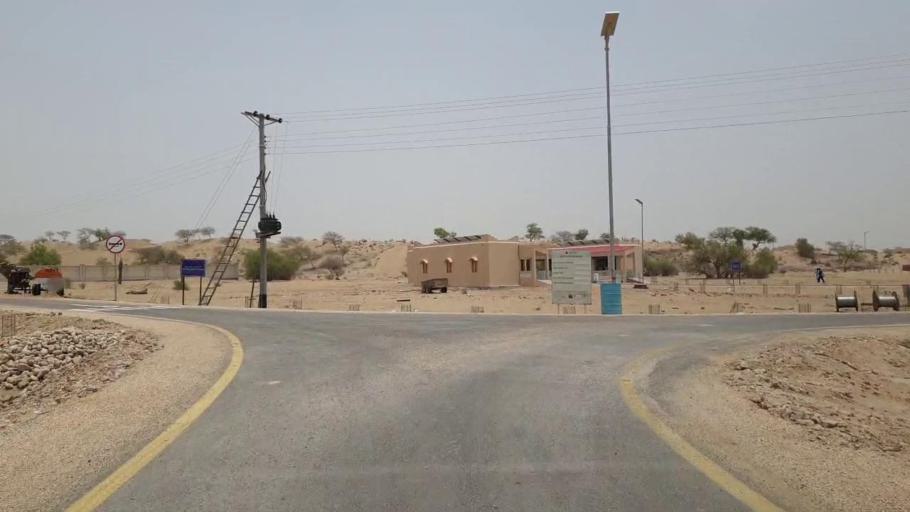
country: PK
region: Sindh
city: Islamkot
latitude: 24.7264
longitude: 70.3239
